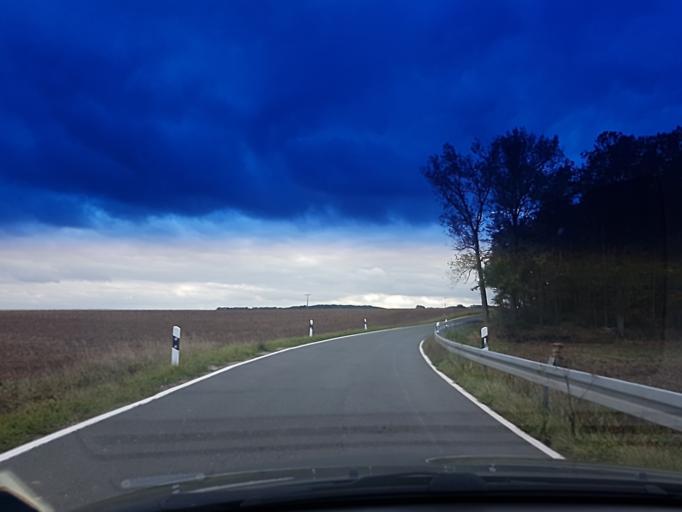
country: DE
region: Bavaria
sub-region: Regierungsbezirk Mittelfranken
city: Hochstadt an der Aisch
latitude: 49.7292
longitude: 10.8367
